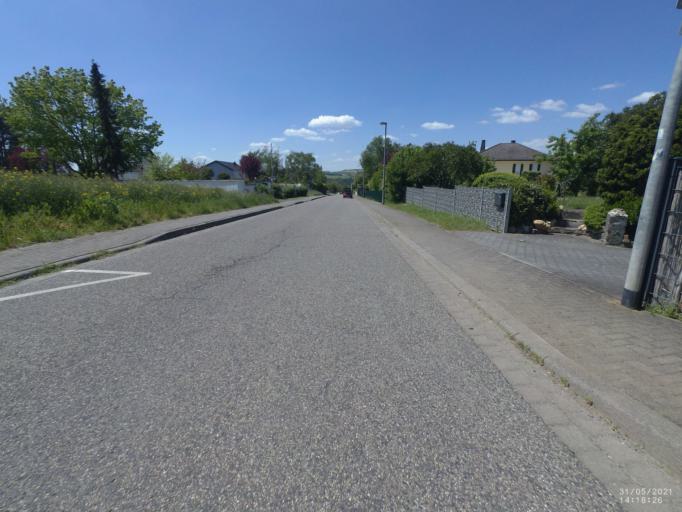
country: DE
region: Rheinland-Pfalz
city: Dieblich
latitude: 50.3075
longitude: 7.4735
